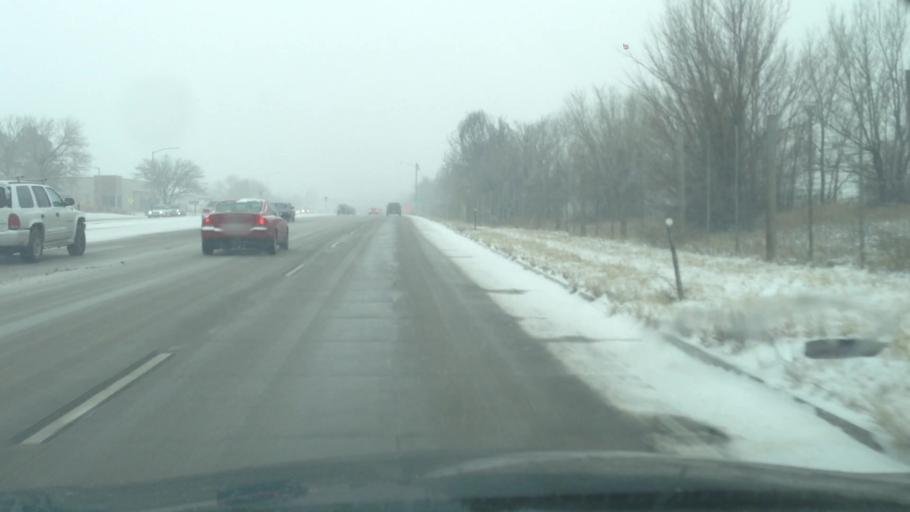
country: US
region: Colorado
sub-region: Arapahoe County
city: Dove Valley
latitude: 39.6429
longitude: -104.8290
